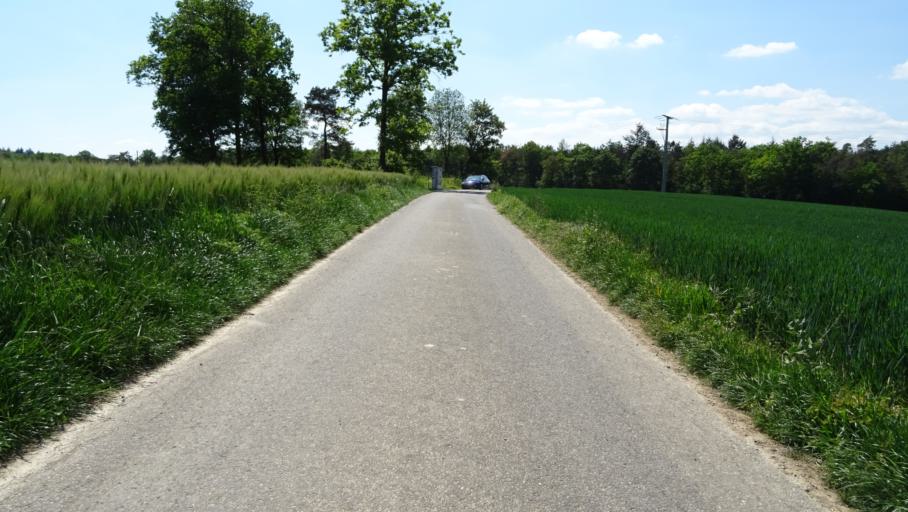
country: DE
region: Baden-Wuerttemberg
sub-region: Karlsruhe Region
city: Buchen
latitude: 49.4982
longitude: 9.3313
